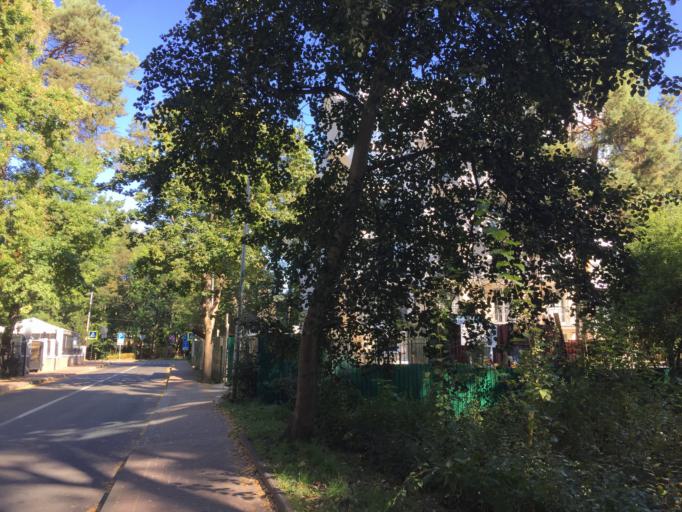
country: RU
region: Kaliningrad
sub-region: Gorod Svetlogorsk
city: Svetlogorsk
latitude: 54.9428
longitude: 20.1631
